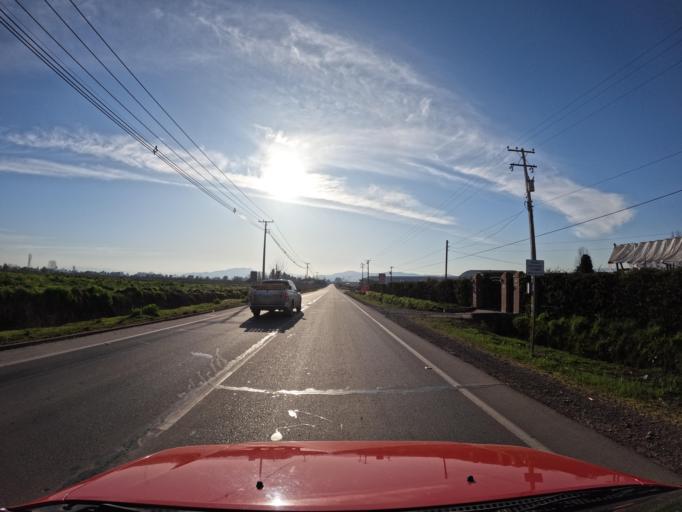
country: CL
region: Maule
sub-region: Provincia de Curico
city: Teno
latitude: -34.8571
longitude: -71.1017
